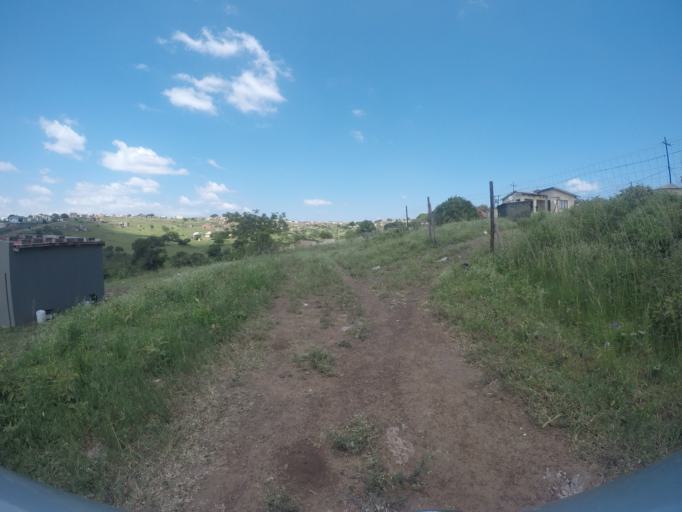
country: ZA
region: KwaZulu-Natal
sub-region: uThungulu District Municipality
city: Empangeni
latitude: -28.6051
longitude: 31.7360
